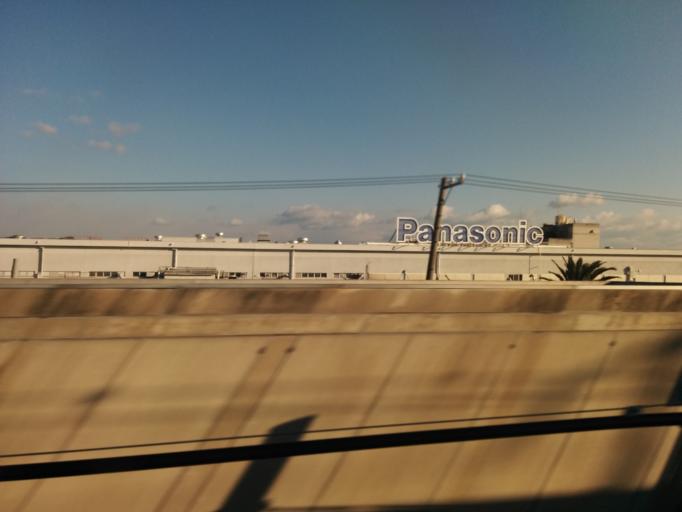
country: JP
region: Shizuoka
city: Kosai-shi
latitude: 34.7137
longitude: 137.4895
